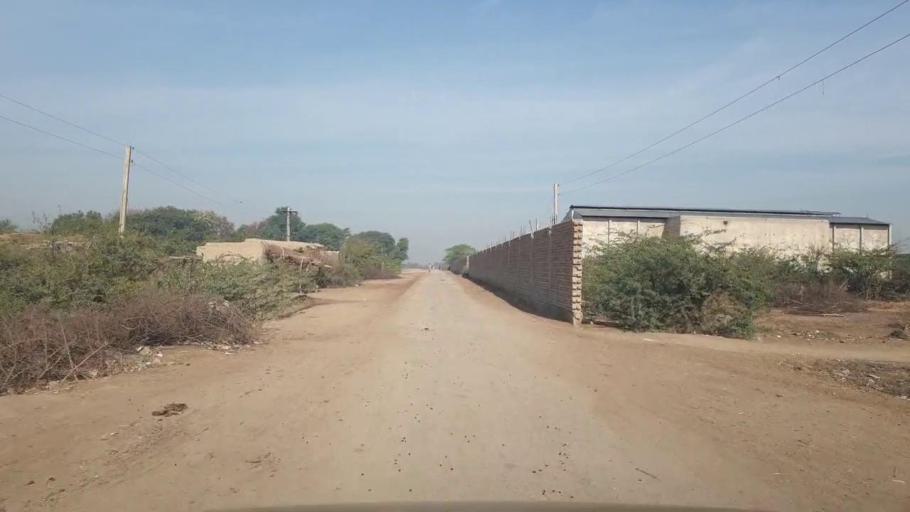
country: PK
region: Sindh
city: Umarkot
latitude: 25.3424
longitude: 69.6926
